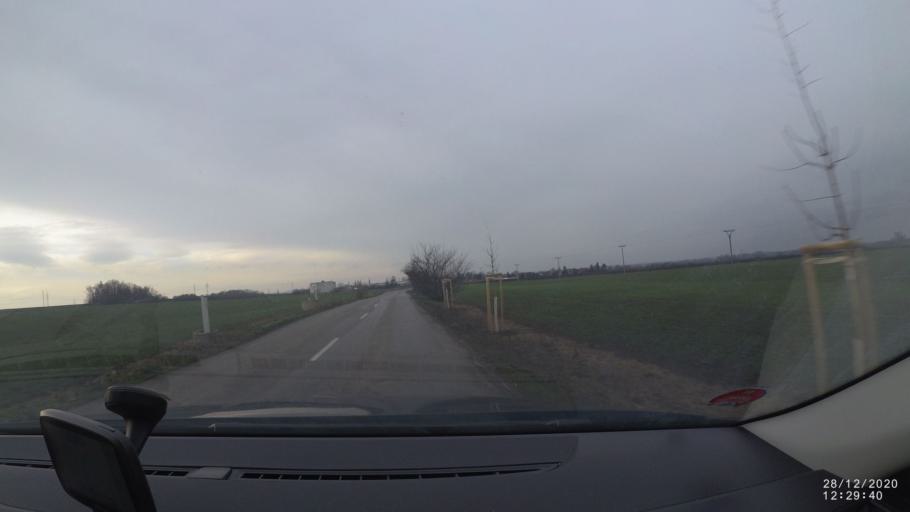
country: CZ
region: Central Bohemia
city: Kostelec nad Labem
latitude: 50.1978
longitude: 14.6089
